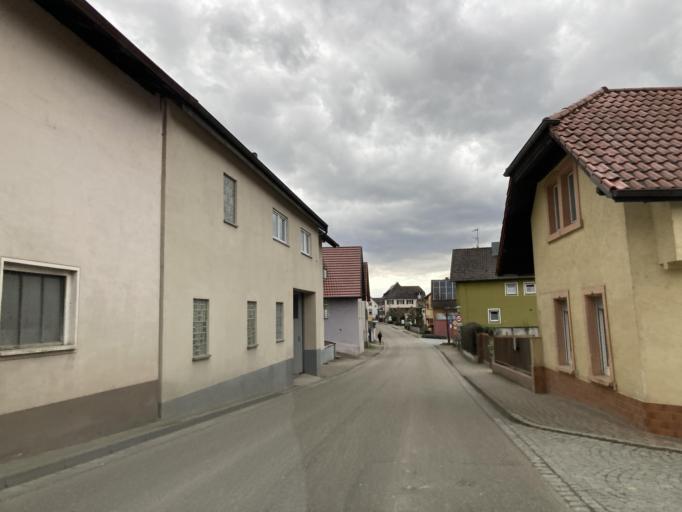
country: DE
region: Baden-Wuerttemberg
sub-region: Freiburg Region
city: Vogtsburg
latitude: 48.0957
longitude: 7.6584
